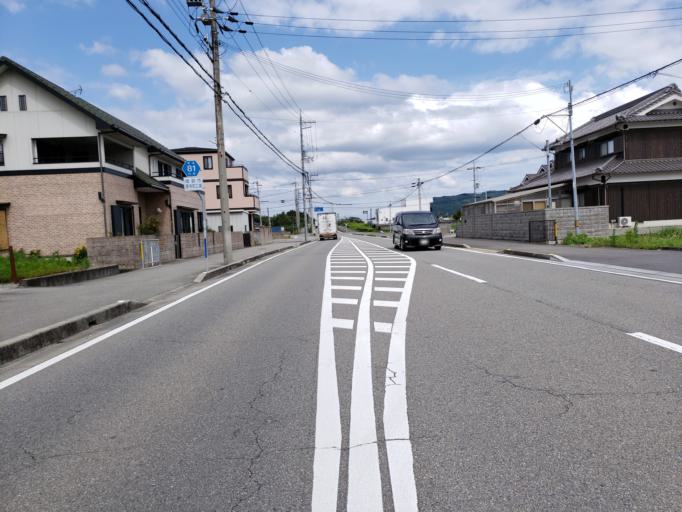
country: JP
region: Hyogo
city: Himeji
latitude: 34.9140
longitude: 134.7427
